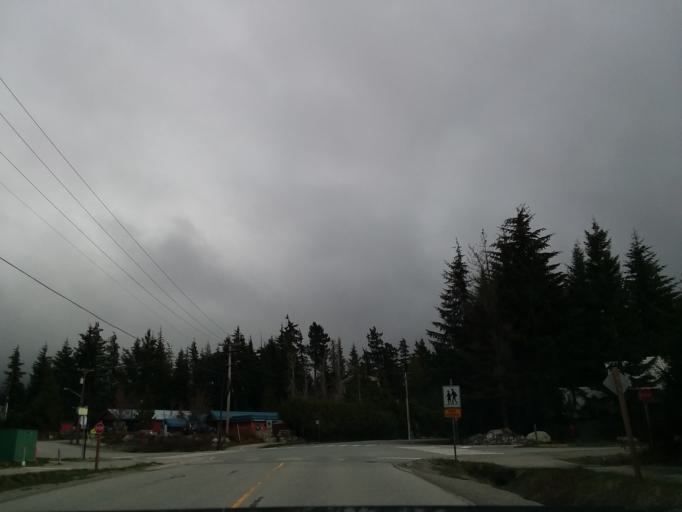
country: CA
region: British Columbia
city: Whistler
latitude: 50.1247
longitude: -122.9621
